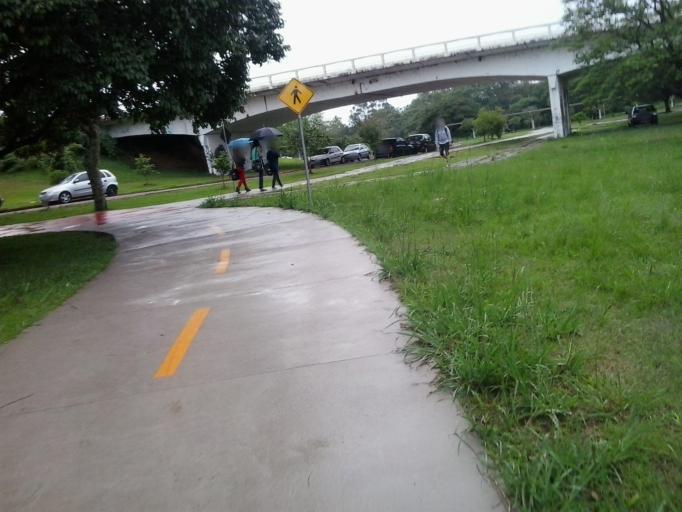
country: BR
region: Rio Grande do Sul
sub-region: Santa Maria
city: Santa Maria
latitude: -29.7170
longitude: -53.7160
